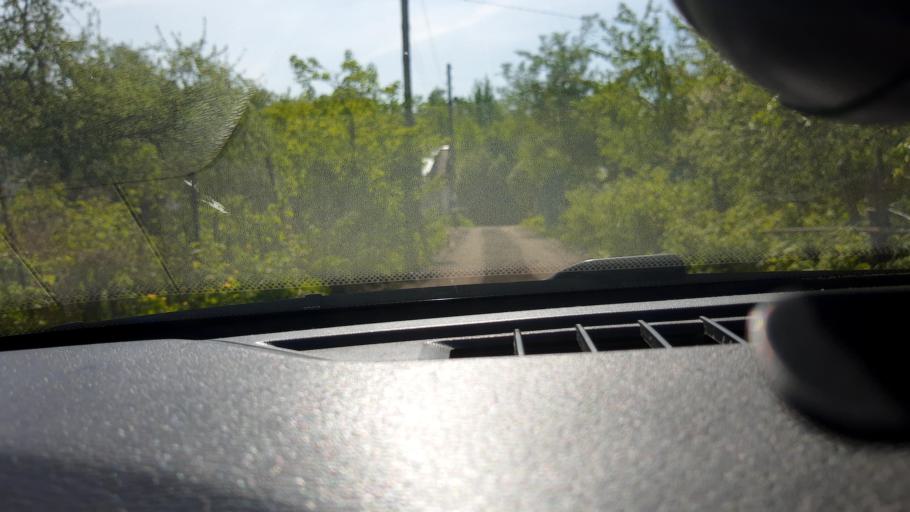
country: RU
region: Nizjnij Novgorod
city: Gorbatovka
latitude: 56.2775
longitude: 43.7879
